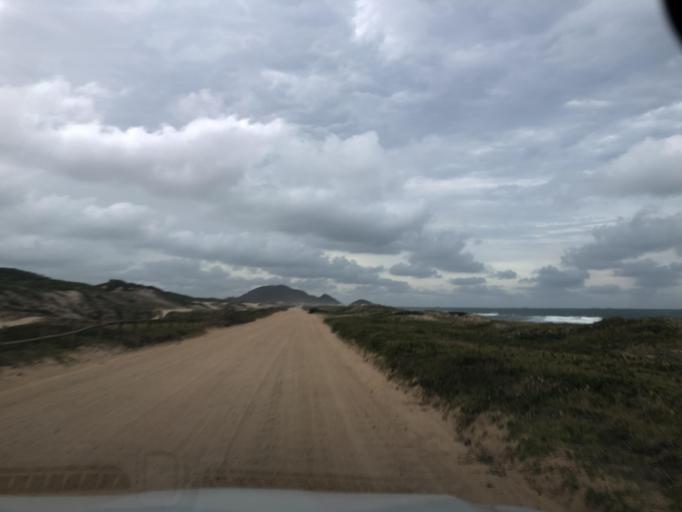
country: BR
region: Santa Catarina
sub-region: Sao Francisco Do Sul
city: Sao Francisco do Sul
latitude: -26.2496
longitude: -48.5125
